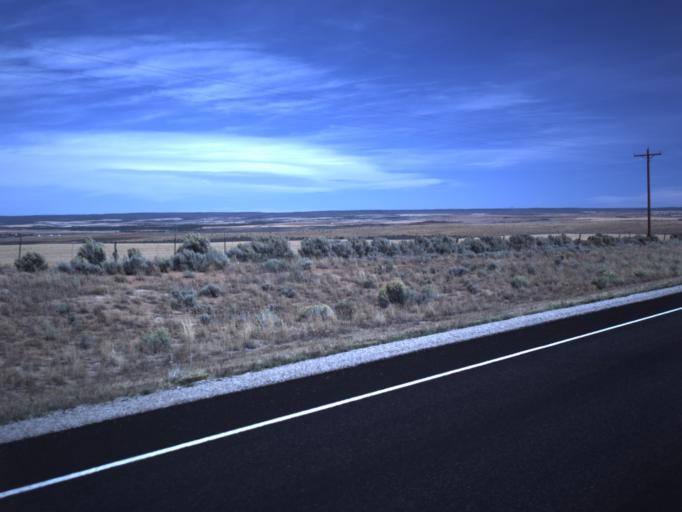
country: US
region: Colorado
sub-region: Dolores County
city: Dove Creek
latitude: 37.8194
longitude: -109.0521
